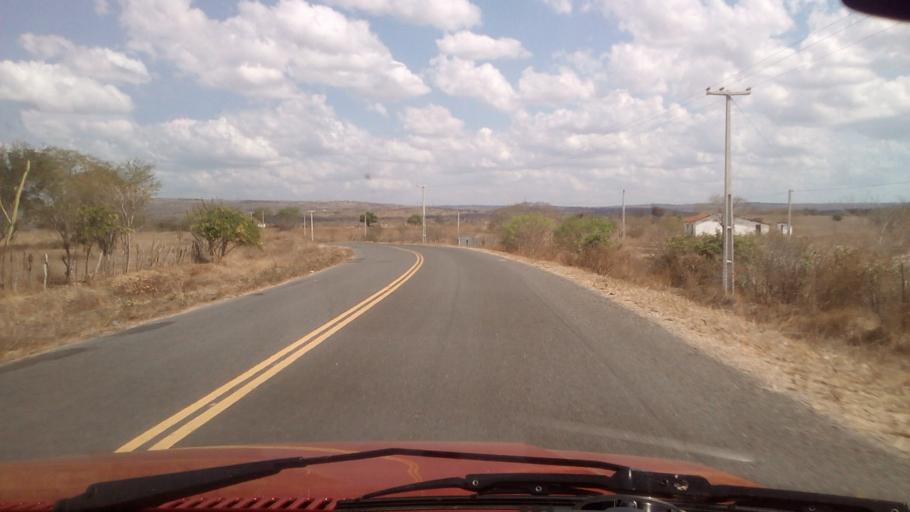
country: BR
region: Paraiba
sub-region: Cacimba De Dentro
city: Cacimba de Dentro
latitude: -6.6733
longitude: -35.7513
